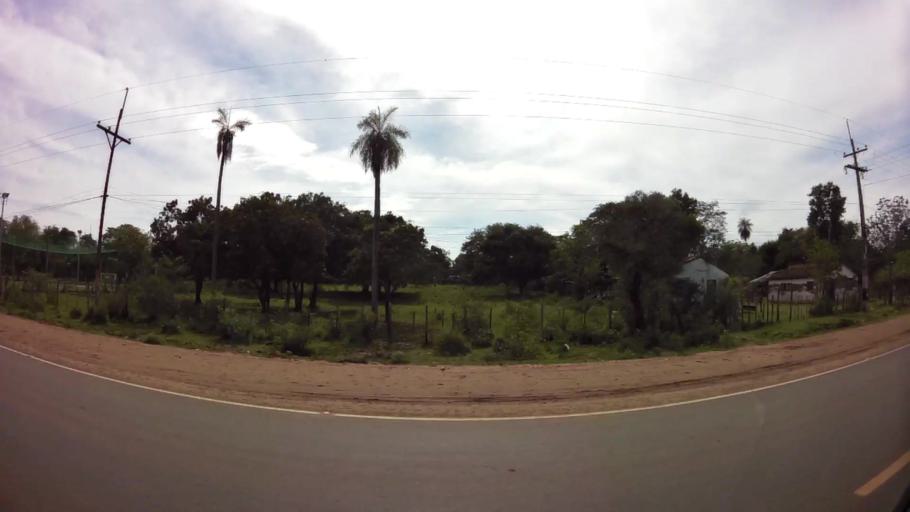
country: PY
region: Presidente Hayes
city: Villa Hayes
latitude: -25.1090
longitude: -57.4901
